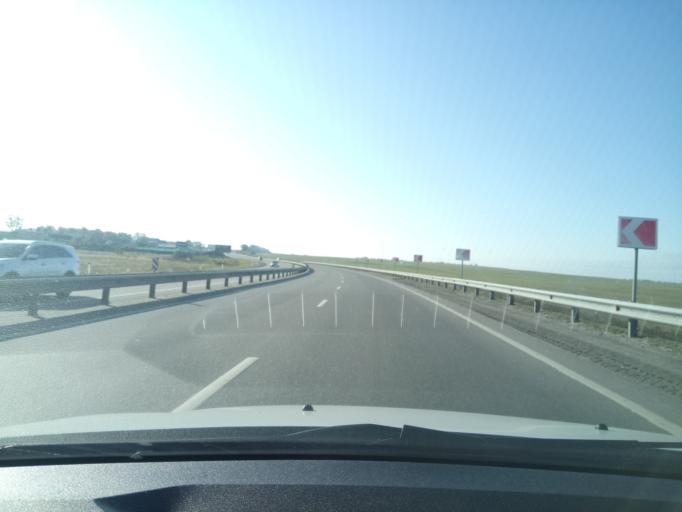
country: RU
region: Nizjnij Novgorod
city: Burevestnik
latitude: 56.1507
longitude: 43.9083
